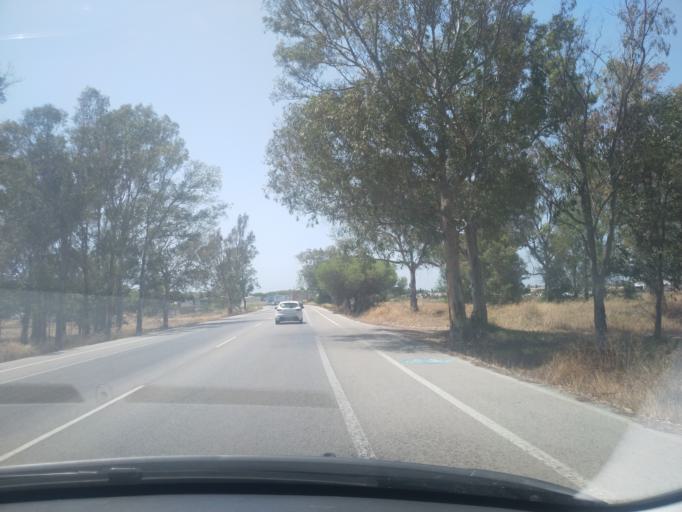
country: ES
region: Andalusia
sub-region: Provincia de Cadiz
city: Chiclana de la Frontera
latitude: 36.3905
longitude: -6.1302
